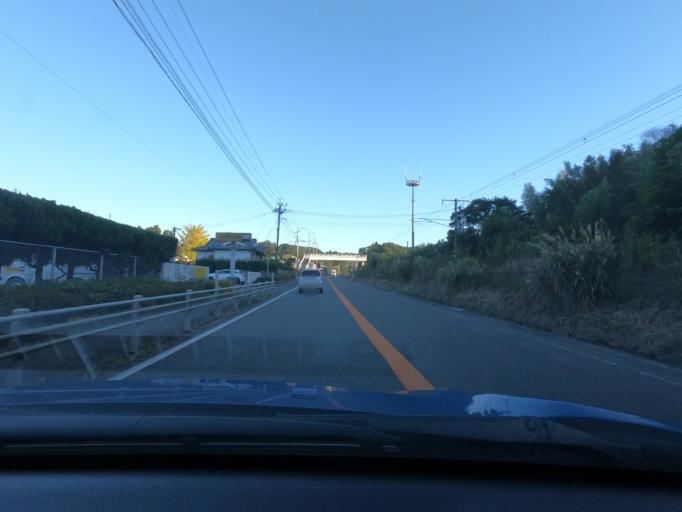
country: JP
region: Kagoshima
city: Satsumasendai
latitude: 31.8503
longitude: 130.2419
